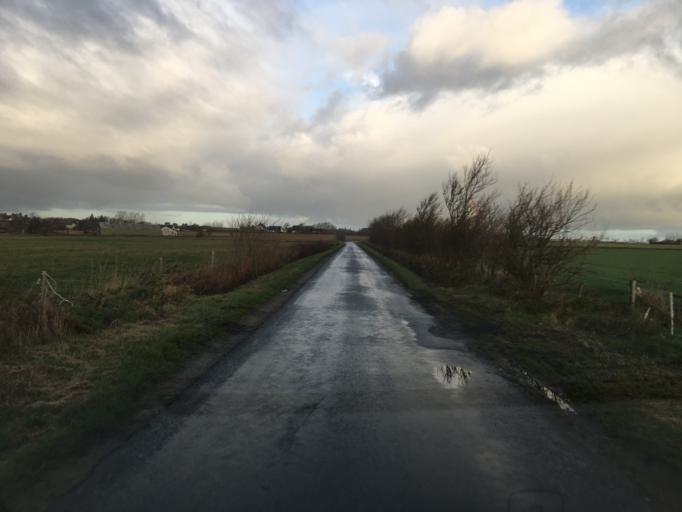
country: DK
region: South Denmark
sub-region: Tonder Kommune
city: Sherrebek
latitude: 55.1508
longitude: 8.8265
